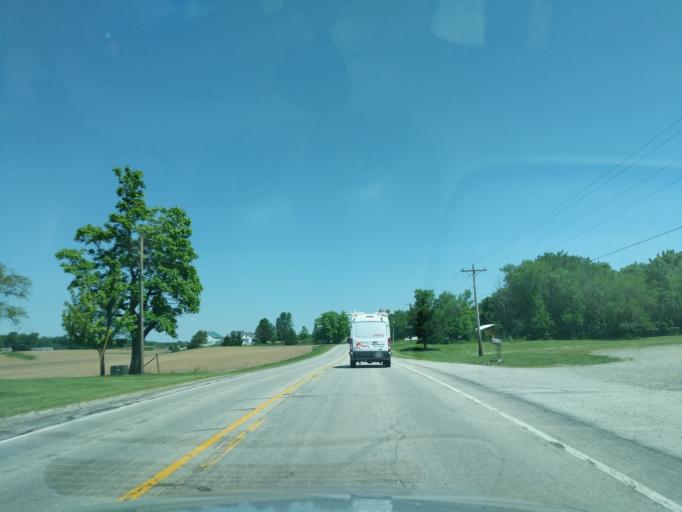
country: US
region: Indiana
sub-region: Whitley County
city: Columbia City
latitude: 41.1796
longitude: -85.4915
